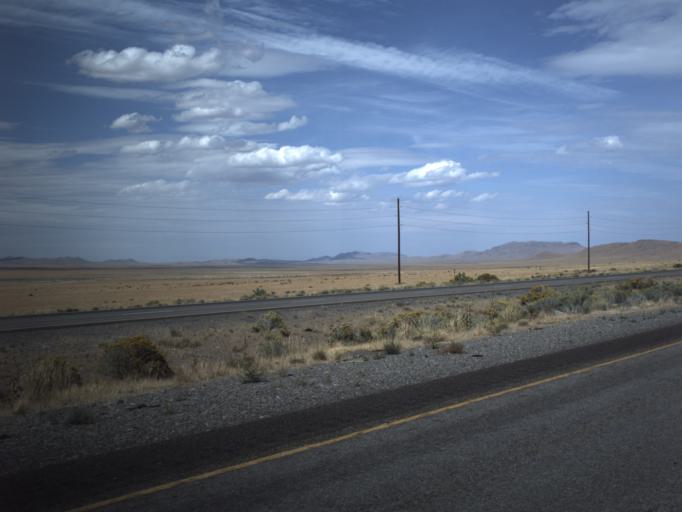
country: US
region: Utah
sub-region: Tooele County
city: Grantsville
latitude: 40.8002
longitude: -112.9428
